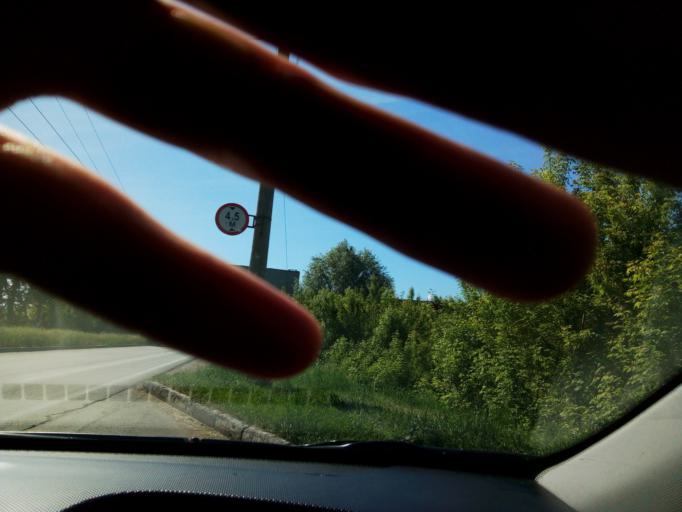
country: RU
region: Chuvashia
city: Novocheboksarsk
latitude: 56.0834
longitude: 47.5041
